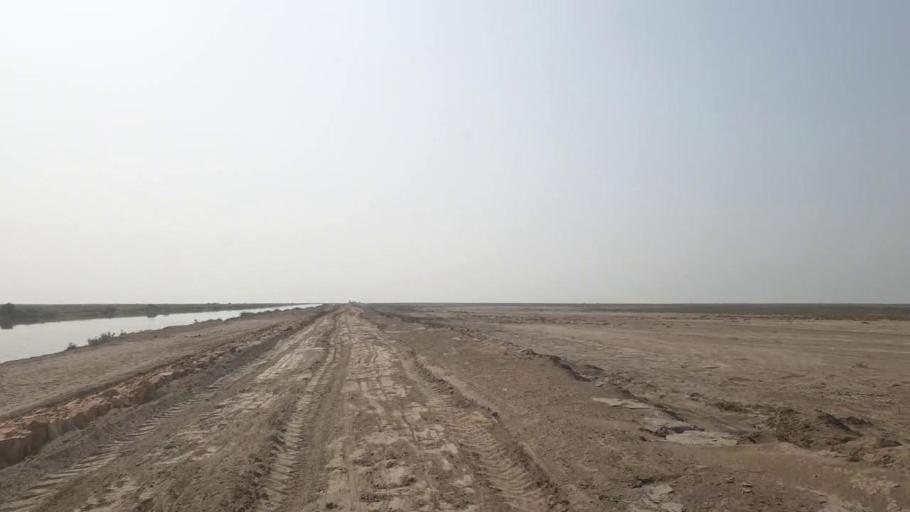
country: PK
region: Sindh
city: Kadhan
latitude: 24.3343
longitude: 68.8404
